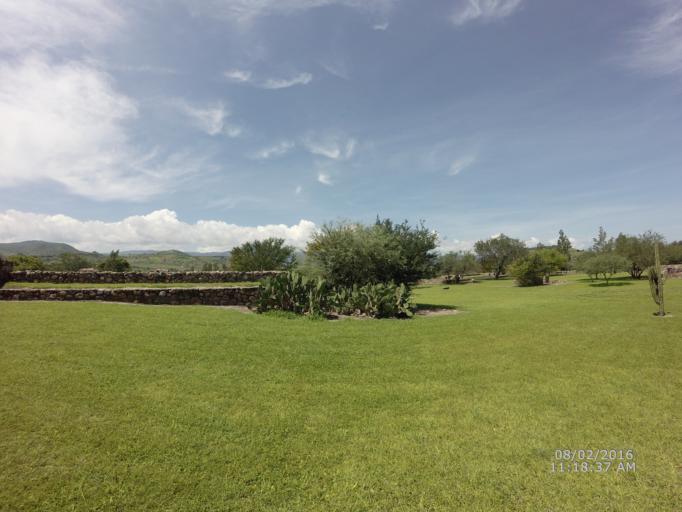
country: MX
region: Nayarit
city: Ixtlan del Rio
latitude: 21.0392
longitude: -104.3442
